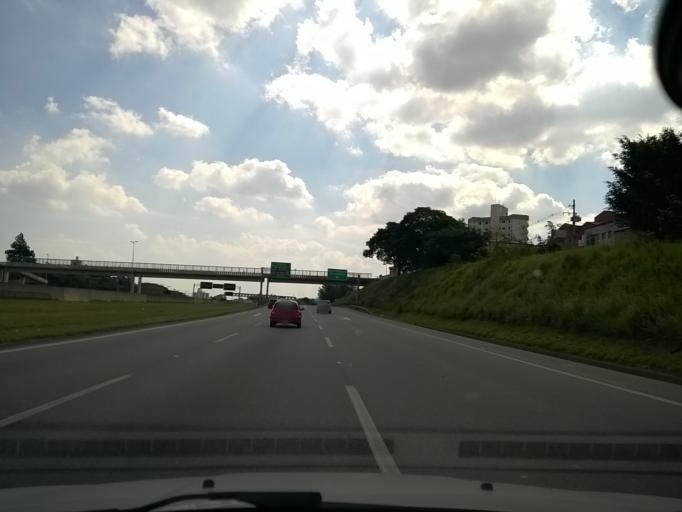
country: BR
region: Sao Paulo
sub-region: Osasco
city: Osasco
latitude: -23.5078
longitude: -46.7406
